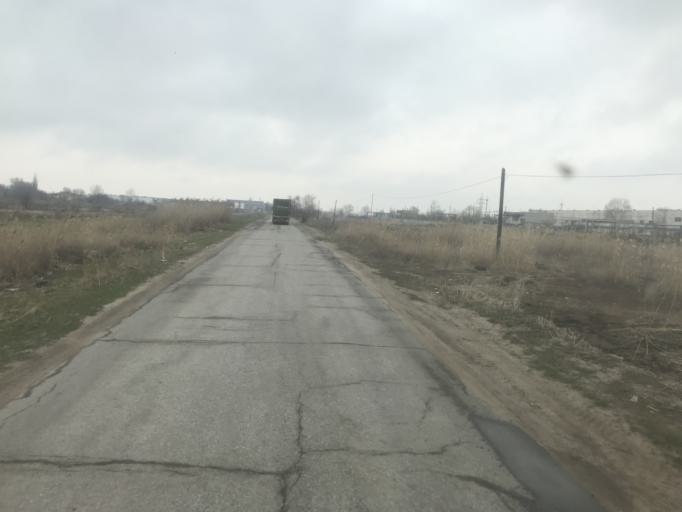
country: RU
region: Volgograd
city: Svetlyy Yar
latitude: 48.5204
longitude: 44.6239
